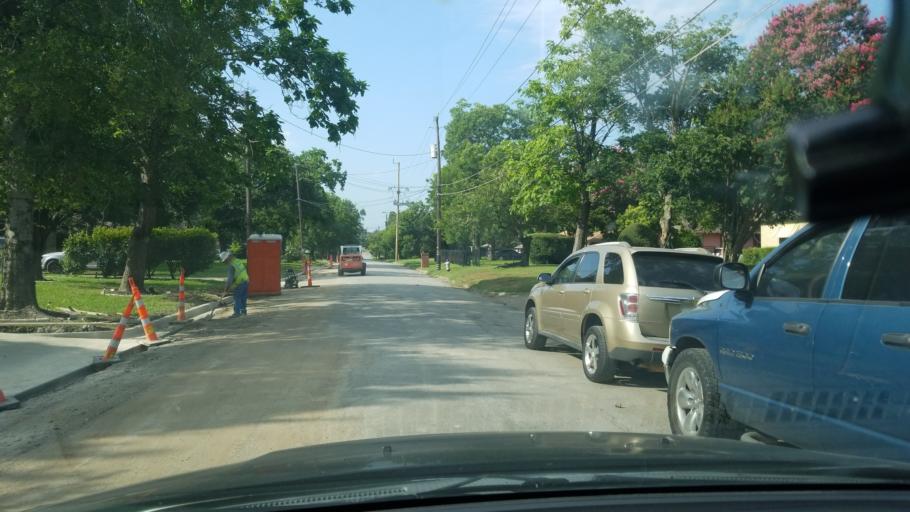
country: US
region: Texas
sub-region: Dallas County
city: Hutchins
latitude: 32.7165
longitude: -96.6930
